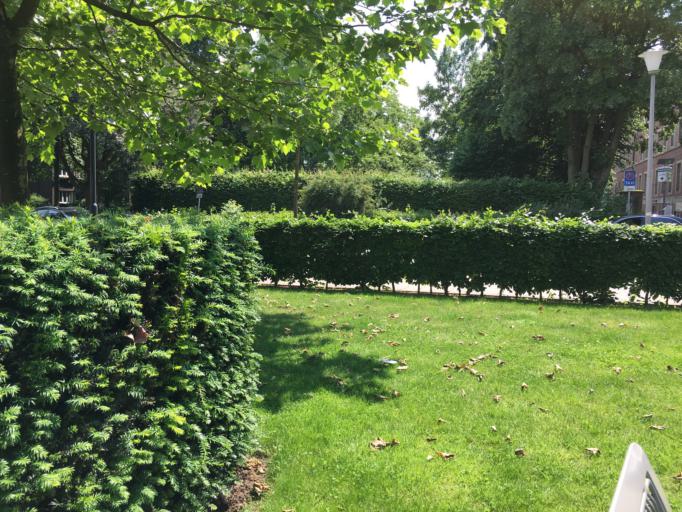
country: DE
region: North Rhine-Westphalia
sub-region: Regierungsbezirk Munster
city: Muenster
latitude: 51.9599
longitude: 7.6487
